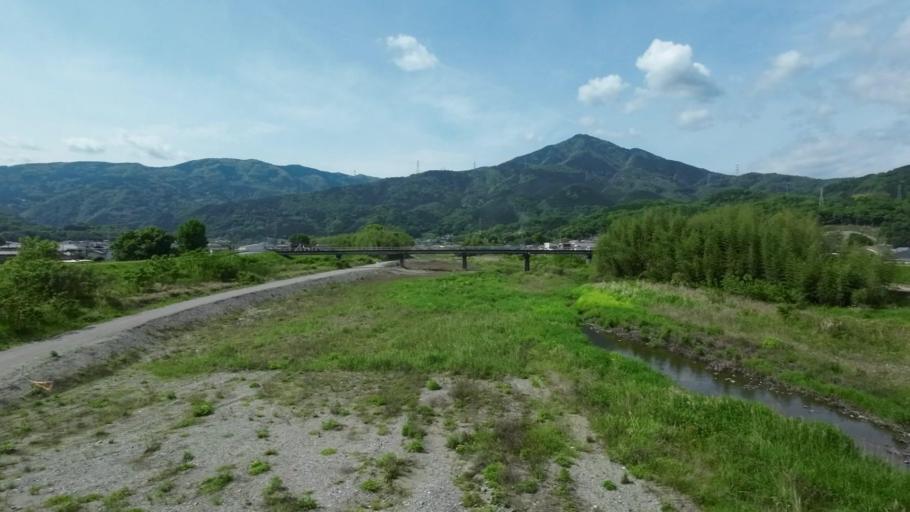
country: JP
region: Tokushima
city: Wakimachi
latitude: 34.0553
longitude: 134.2267
